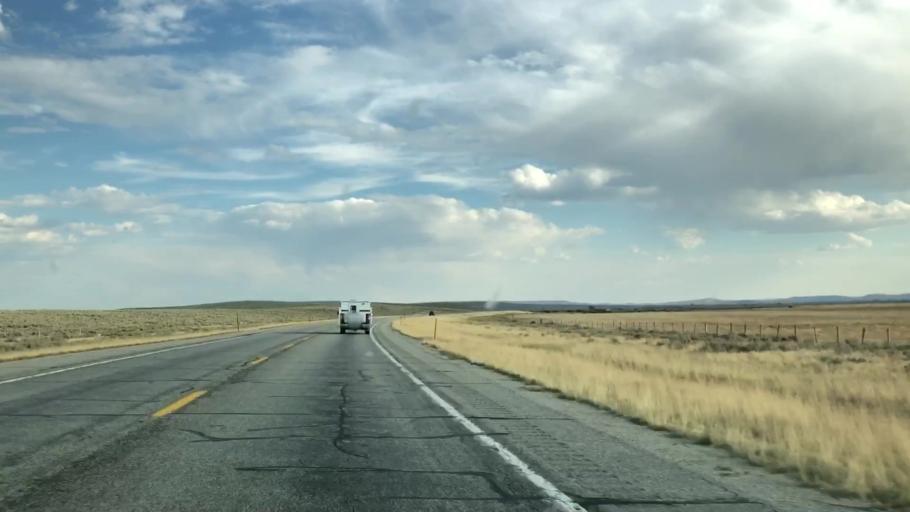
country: US
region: Wyoming
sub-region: Sublette County
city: Pinedale
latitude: 43.0329
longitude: -110.1293
